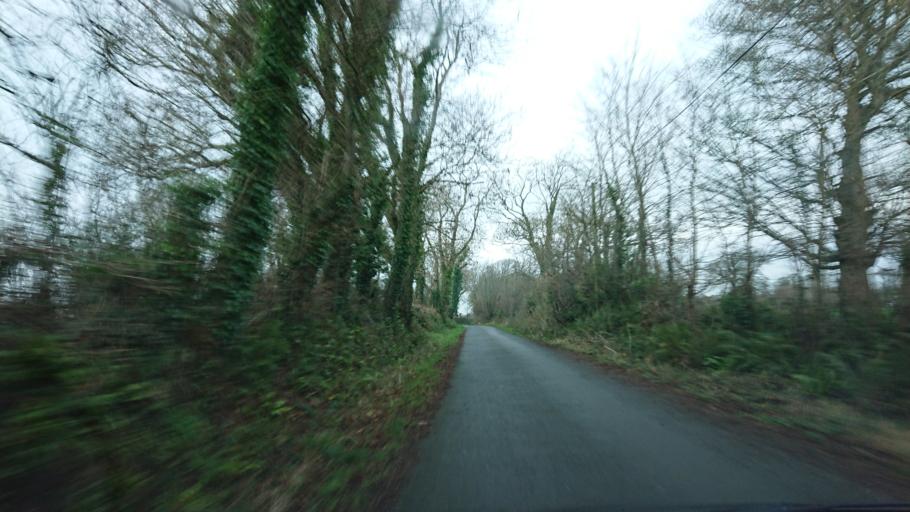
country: IE
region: Munster
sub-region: Waterford
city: Dunmore East
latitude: 52.2032
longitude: -7.0133
